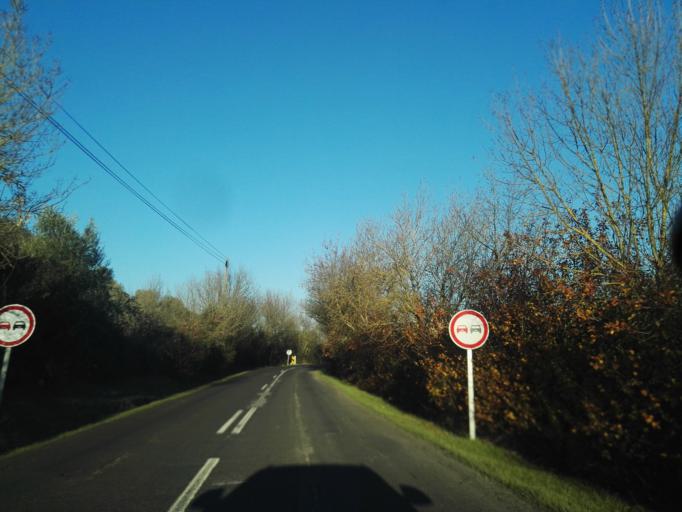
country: PT
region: Santarem
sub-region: Alpiarca
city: Alpiarca
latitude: 39.3234
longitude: -8.5967
